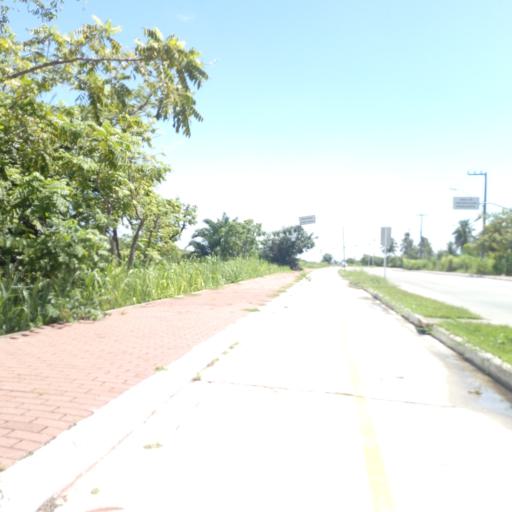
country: BR
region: Pernambuco
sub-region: Sirinhaem
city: Sirinhaem
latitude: -8.5202
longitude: -35.0100
